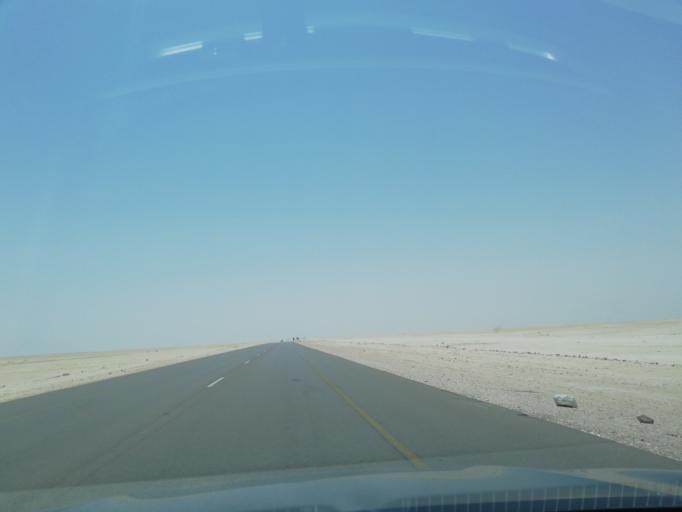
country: OM
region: Al Wusta
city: Hayma'
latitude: 20.2097
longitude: 56.5520
